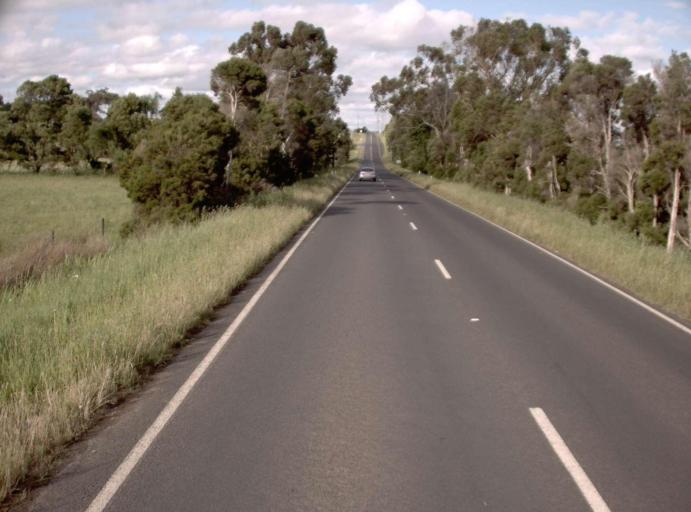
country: AU
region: Victoria
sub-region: Baw Baw
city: Warragul
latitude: -38.4902
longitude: 145.9314
